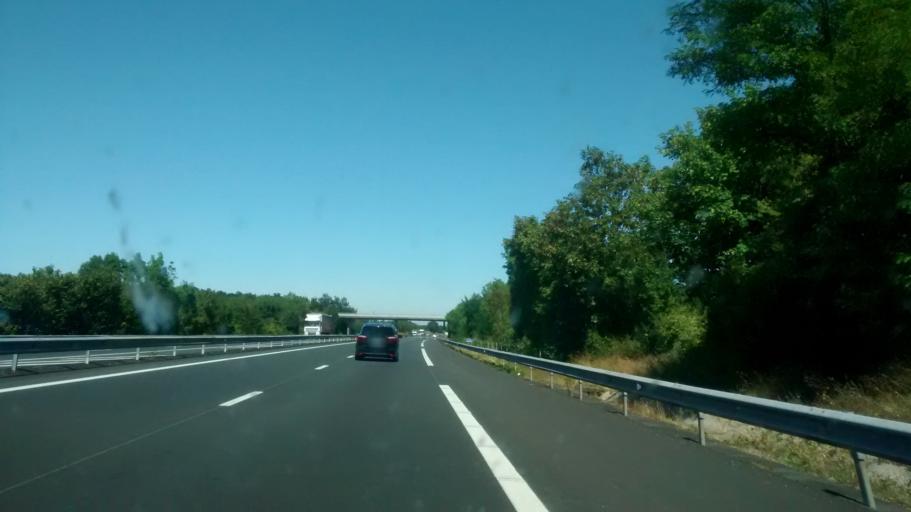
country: FR
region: Poitou-Charentes
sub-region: Departement des Deux-Sevres
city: Beauvoir-sur-Niort
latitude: 46.1027
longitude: -0.5353
